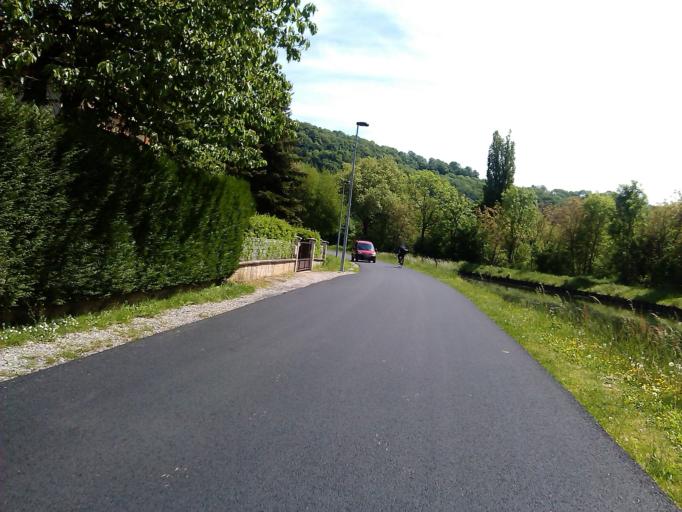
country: FR
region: Franche-Comte
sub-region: Departement du Doubs
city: Avanne-Aveney
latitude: 47.1943
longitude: 5.9594
